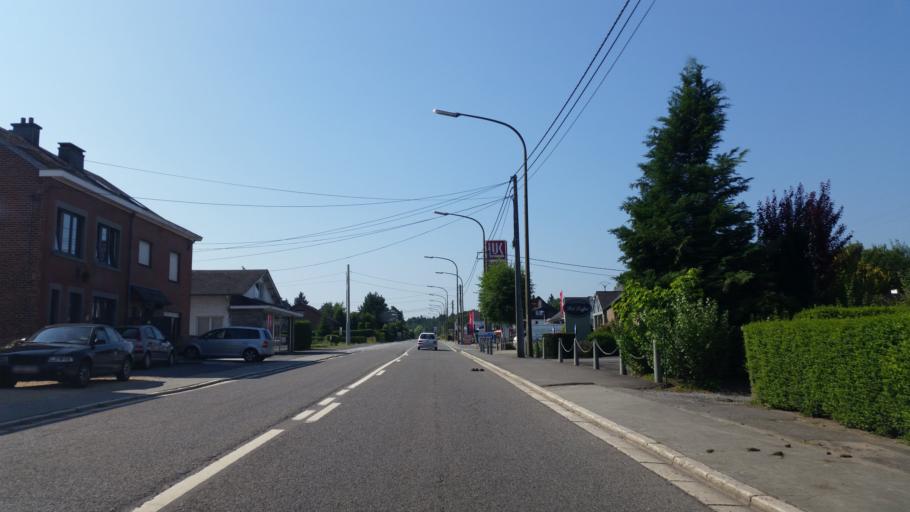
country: BE
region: Wallonia
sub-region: Province du Luxembourg
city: Durbuy
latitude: 50.3452
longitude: 5.4878
